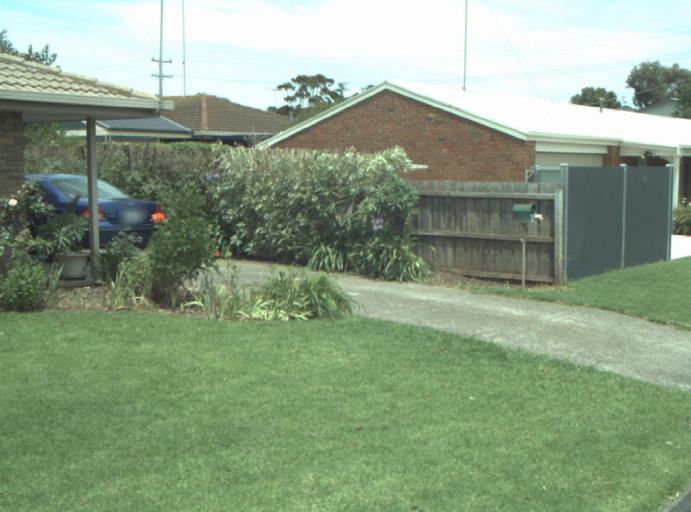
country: AU
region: Victoria
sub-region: Greater Geelong
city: Clifton Springs
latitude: -38.1580
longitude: 144.5515
